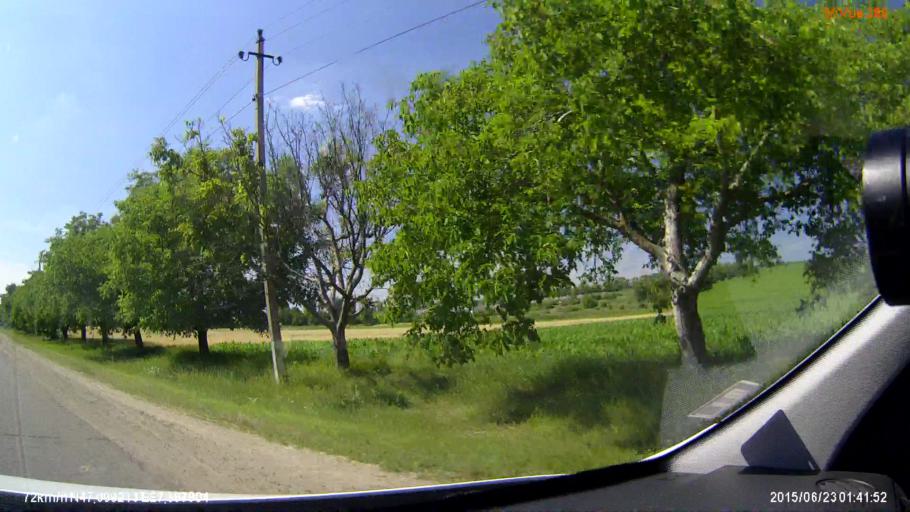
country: RO
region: Iasi
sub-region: Comuna Golaesti
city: Golaesti
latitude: 47.3092
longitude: 27.6982
